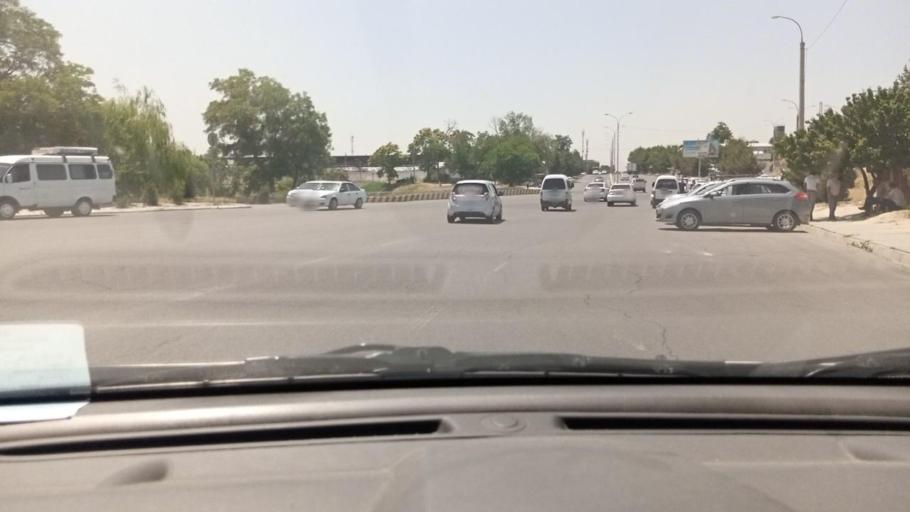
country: UZ
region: Toshkent Shahri
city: Tashkent
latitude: 41.2533
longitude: 69.2162
